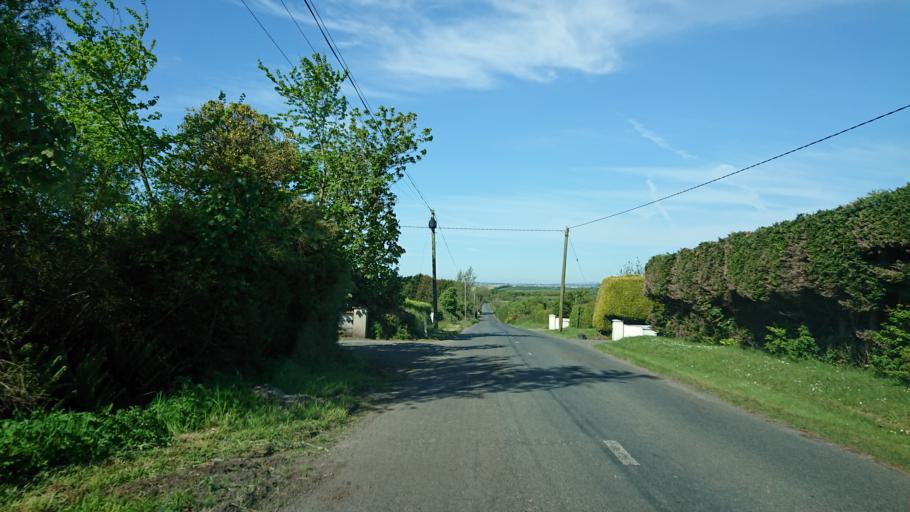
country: IE
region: Munster
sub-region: Waterford
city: Dunmore East
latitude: 52.1775
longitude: -7.0211
